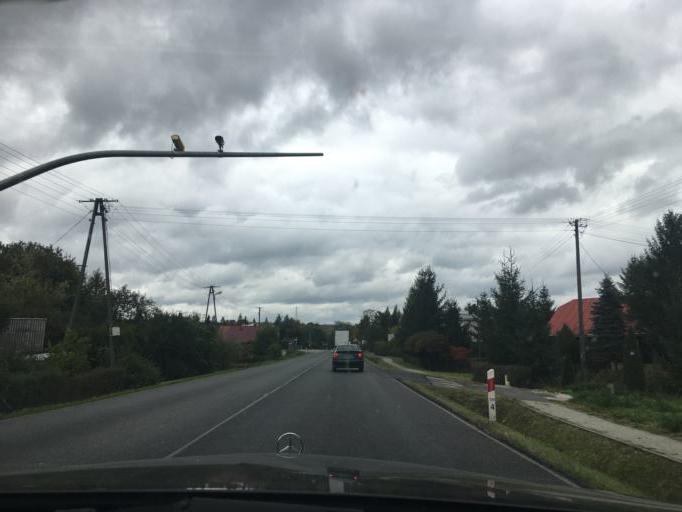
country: PL
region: Subcarpathian Voivodeship
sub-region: Powiat krosnienski
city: Kroscienko Wyzne
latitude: 49.6737
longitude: 21.8491
